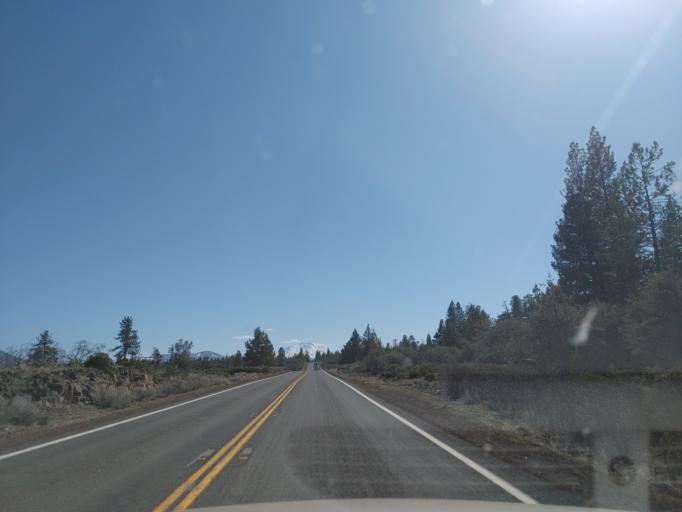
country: US
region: California
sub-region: Shasta County
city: Burney
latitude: 40.6942
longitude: -121.4186
